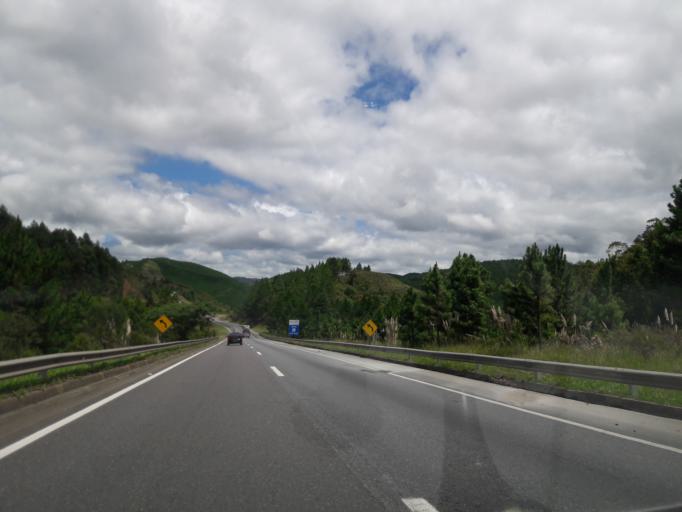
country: BR
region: Parana
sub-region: Campina Grande Do Sul
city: Campina Grande do Sul
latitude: -25.1002
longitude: -48.8225
